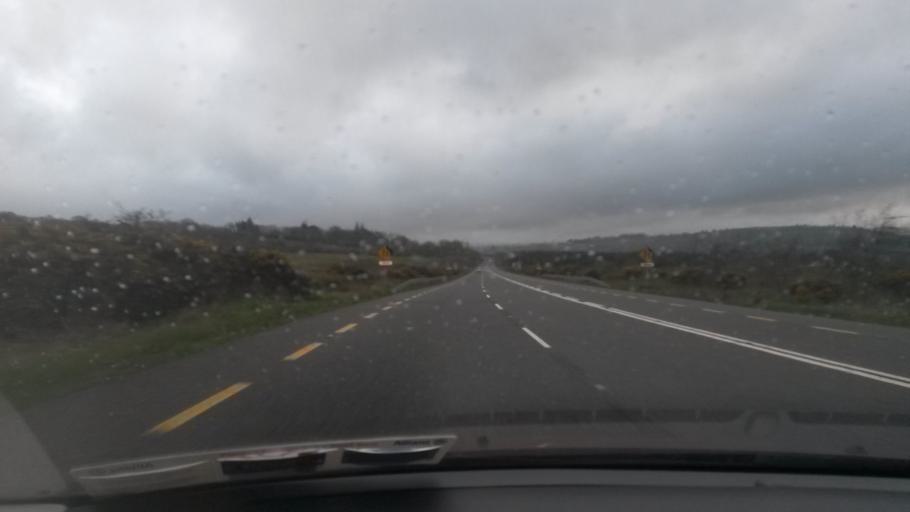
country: IE
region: Munster
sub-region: County Limerick
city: Abbeyfeale
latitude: 52.3477
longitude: -9.3352
